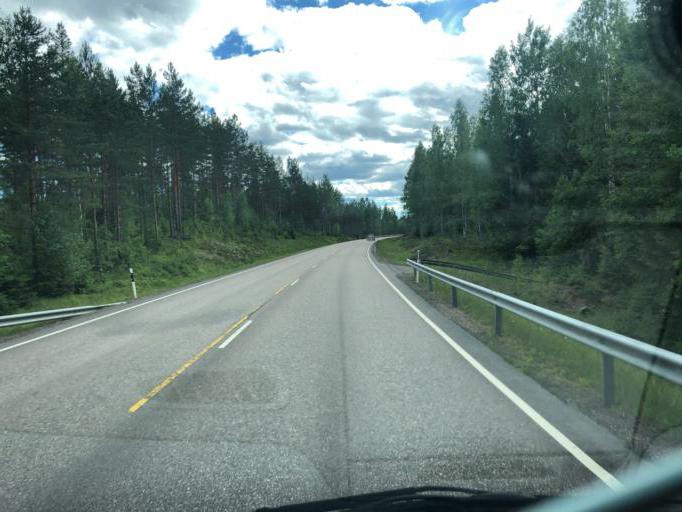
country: FI
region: Southern Savonia
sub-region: Mikkeli
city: Maentyharju
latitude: 61.1017
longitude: 27.0995
